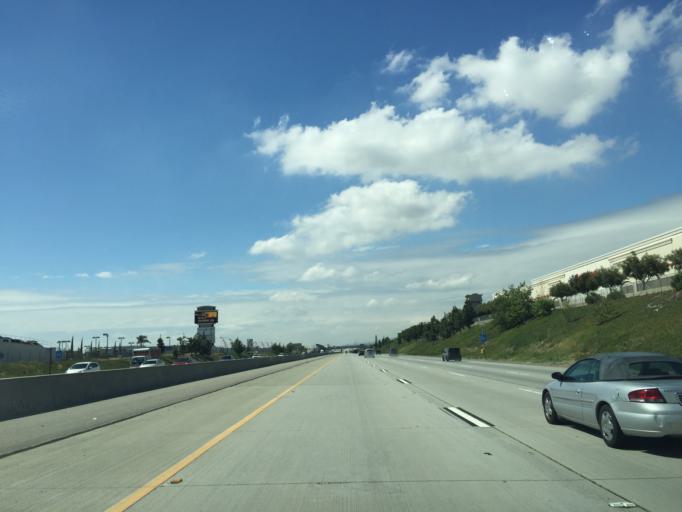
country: US
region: California
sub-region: San Bernardino County
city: Fontana
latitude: 34.1365
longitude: -117.4421
